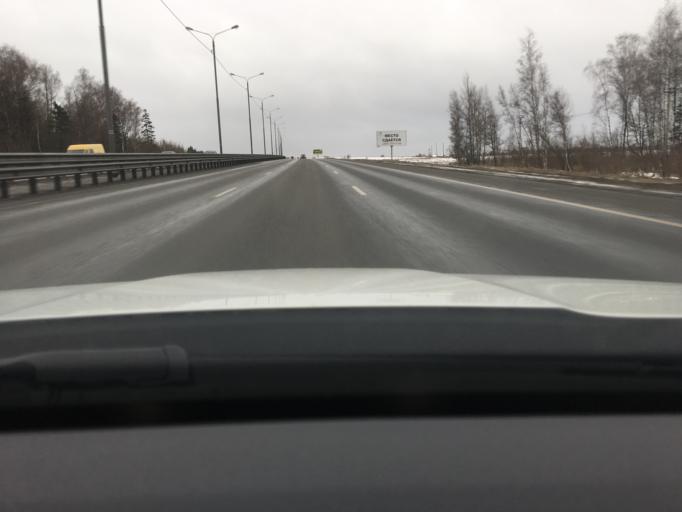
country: RU
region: Moskovskaya
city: Novyy Byt
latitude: 55.0667
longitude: 37.5670
